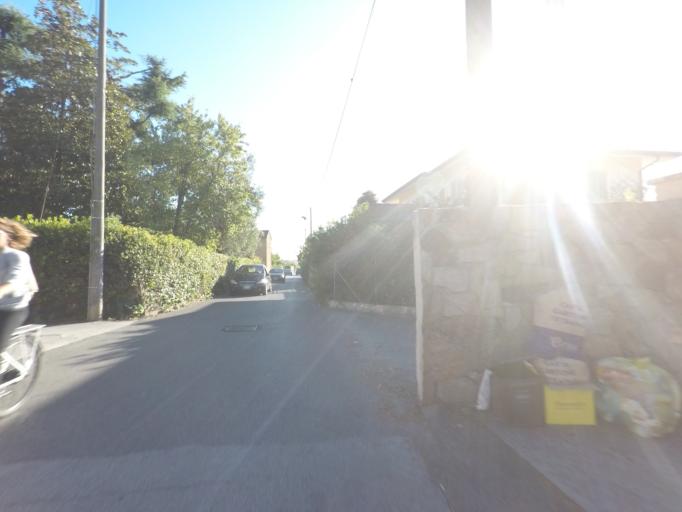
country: IT
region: Tuscany
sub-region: Provincia di Massa-Carrara
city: Capanne-Prato-Cinquale
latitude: 44.0066
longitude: 10.1539
